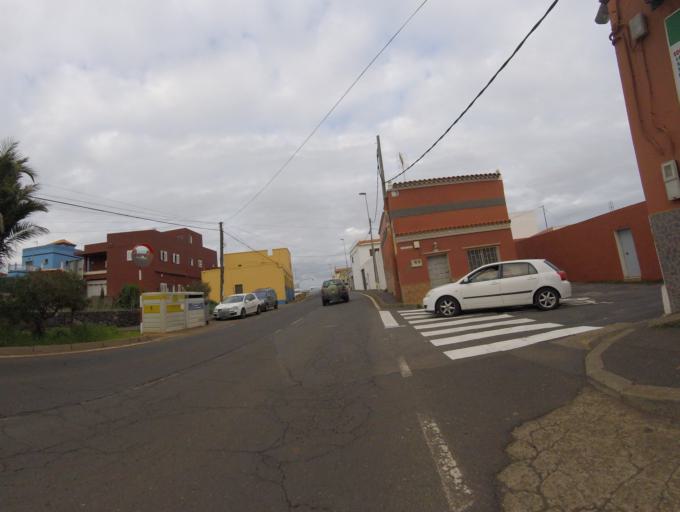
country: ES
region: Canary Islands
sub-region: Provincia de Santa Cruz de Tenerife
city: La Laguna
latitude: 28.4459
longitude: -16.3320
